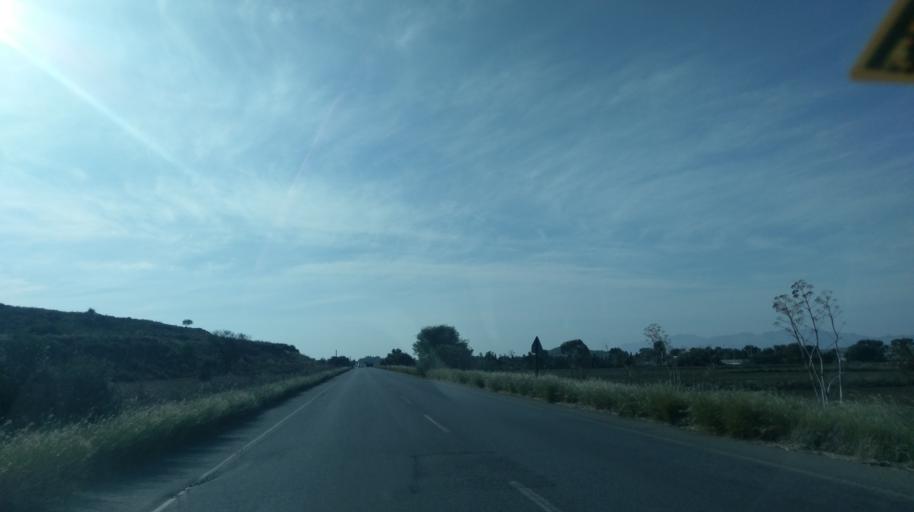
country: CY
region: Ammochostos
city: Lefkonoiko
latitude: 35.2681
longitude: 33.8086
